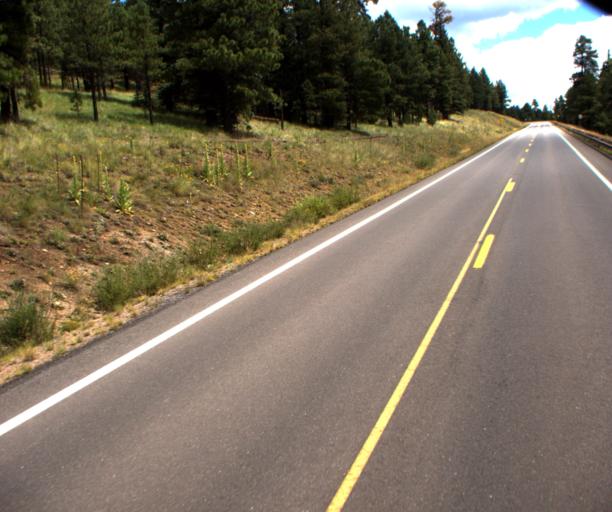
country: US
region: Arizona
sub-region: Apache County
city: Eagar
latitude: 33.9626
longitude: -109.5032
